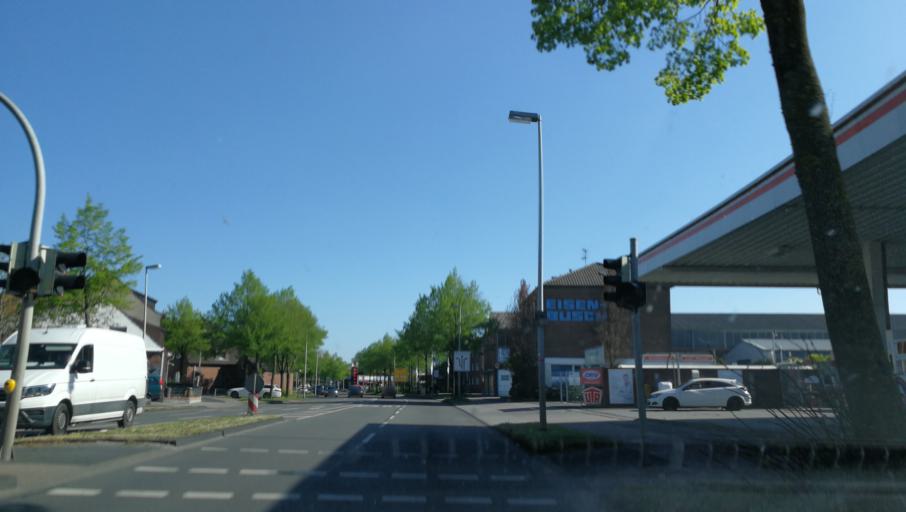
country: DE
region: North Rhine-Westphalia
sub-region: Regierungsbezirk Munster
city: Rheine
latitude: 52.2730
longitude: 7.4408
